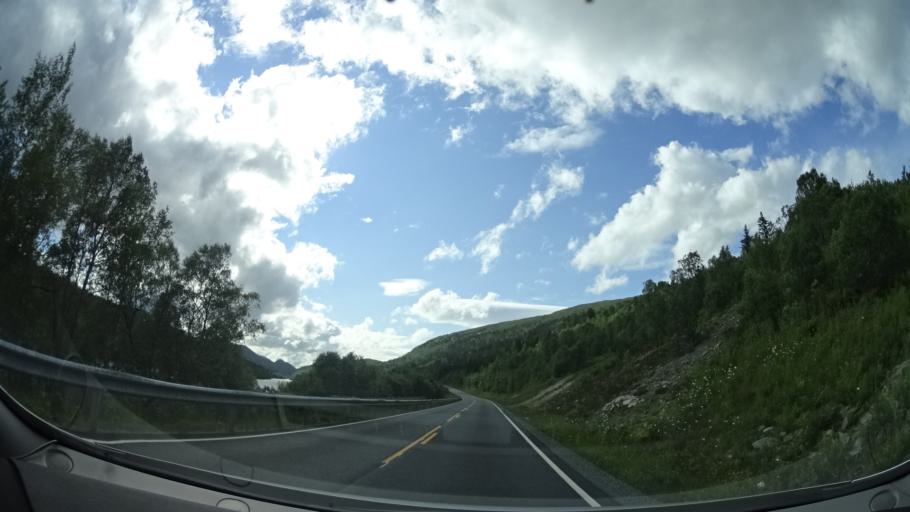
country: NO
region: More og Romsdal
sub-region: Rindal
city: Rindal
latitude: 63.2301
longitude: 9.3375
